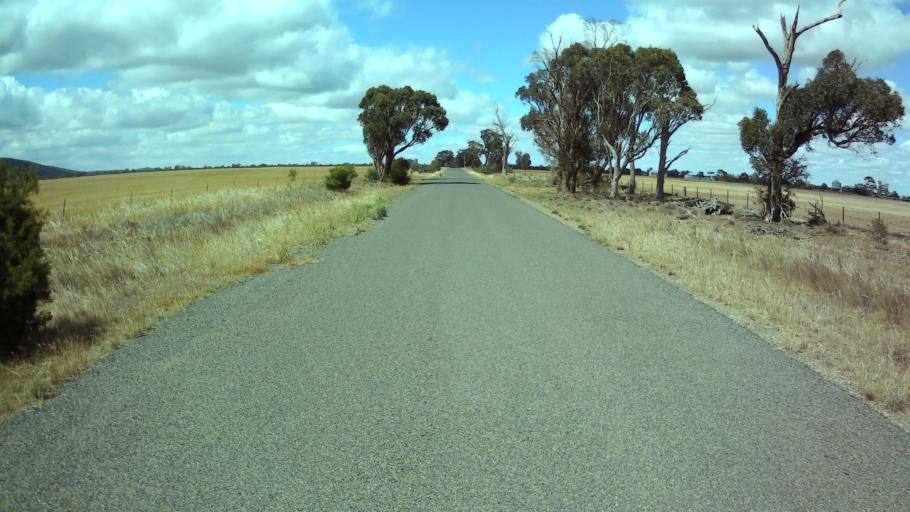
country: AU
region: New South Wales
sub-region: Weddin
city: Grenfell
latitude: -33.8765
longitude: 147.9253
